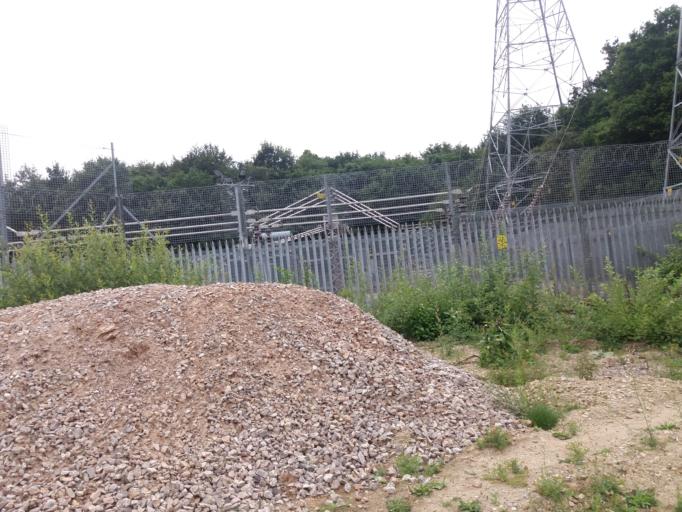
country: GB
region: England
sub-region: Lancashire
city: Preston
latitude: 53.7576
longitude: -2.7329
